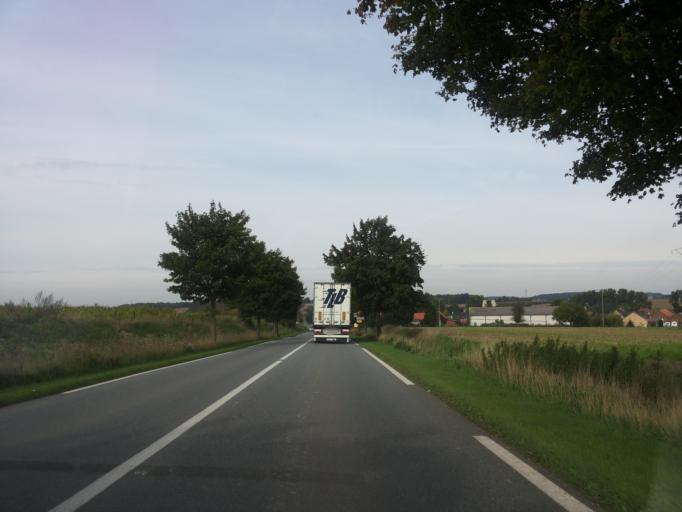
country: FR
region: Nord-Pas-de-Calais
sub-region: Departement du Pas-de-Calais
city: Biache-Saint-Vaast
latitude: 50.2443
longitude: 2.9559
